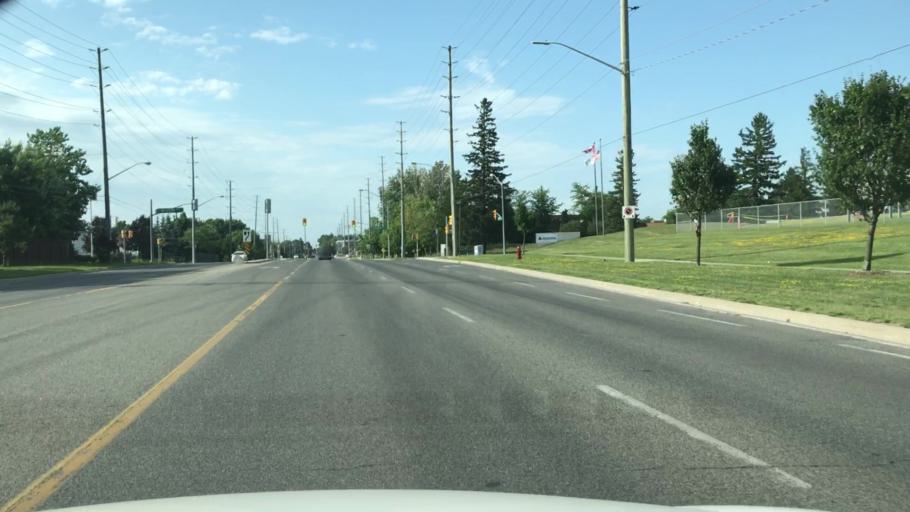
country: CA
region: Ontario
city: Newmarket
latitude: 44.0352
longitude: -79.4505
